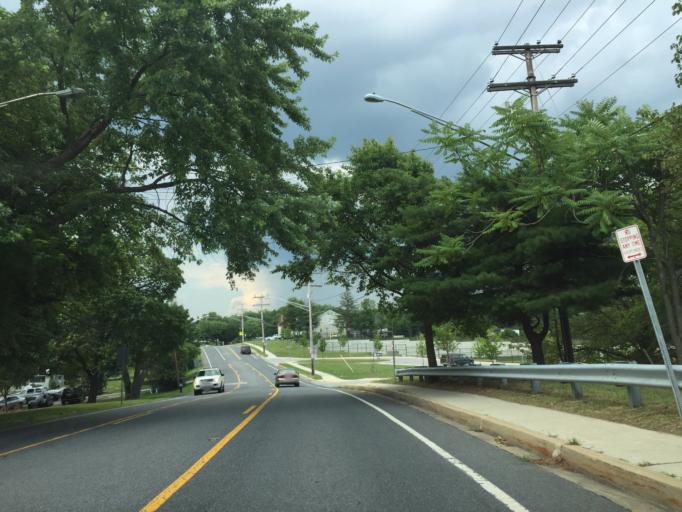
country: US
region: Maryland
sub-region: Montgomery County
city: Fairland
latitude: 39.0893
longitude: -76.9480
